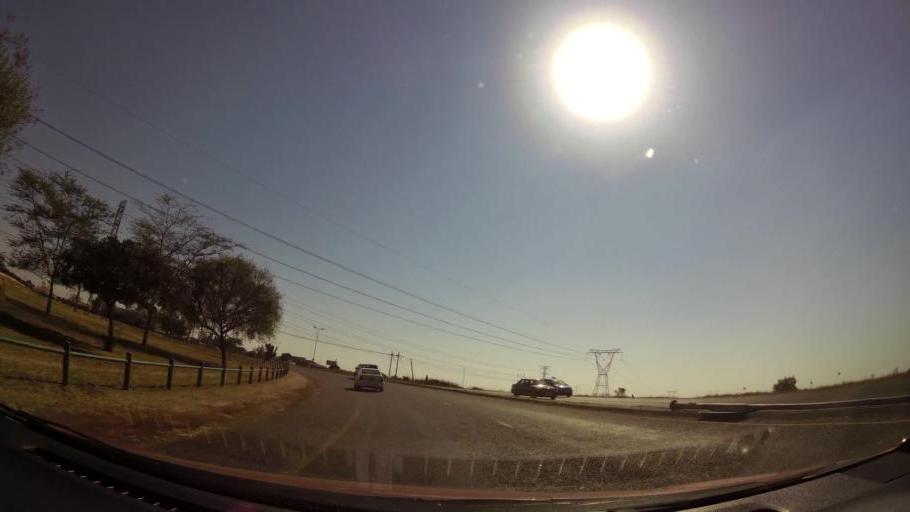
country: ZA
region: Gauteng
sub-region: City of Tshwane Metropolitan Municipality
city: Mabopane
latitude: -25.5322
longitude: 28.1164
